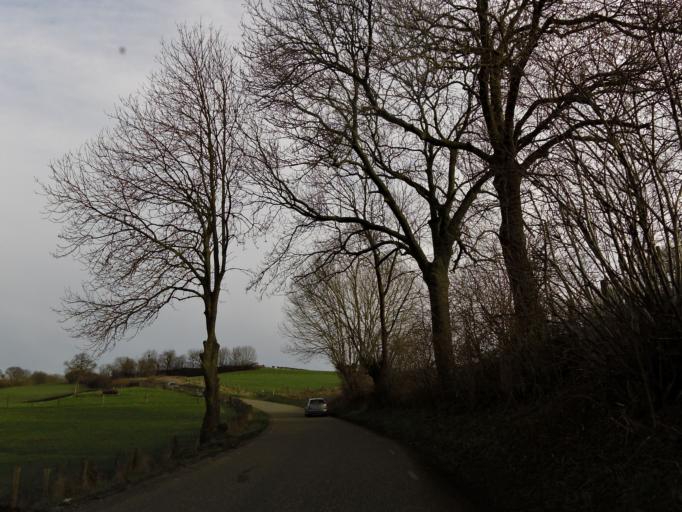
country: NL
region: Limburg
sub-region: Gemeente Voerendaal
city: Ubachsberg
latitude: 50.8324
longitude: 5.9380
